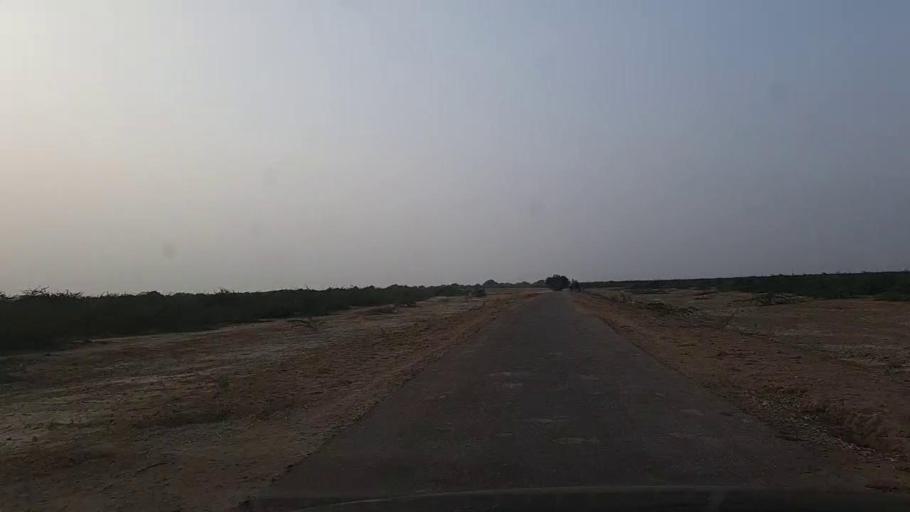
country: PK
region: Sindh
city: Gharo
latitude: 24.7822
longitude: 67.7290
